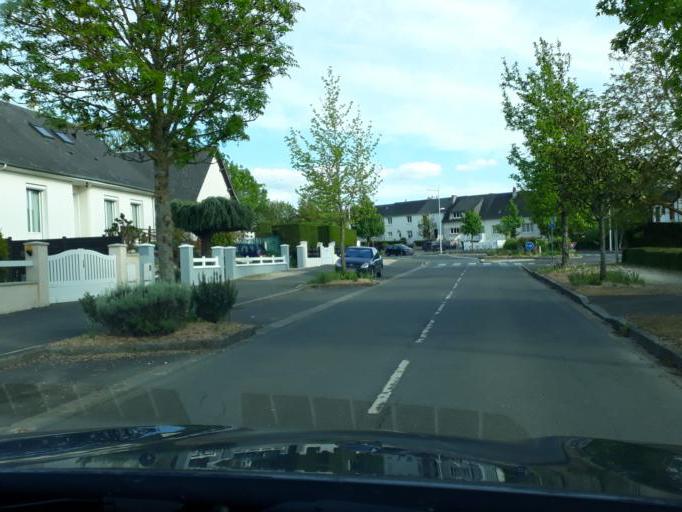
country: FR
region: Centre
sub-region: Departement du Loiret
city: Ingre
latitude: 47.9172
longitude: 1.8342
